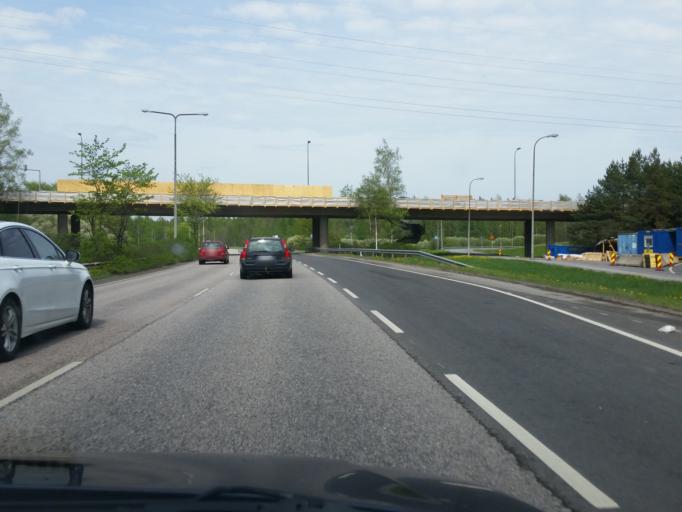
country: FI
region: Uusimaa
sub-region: Helsinki
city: Helsinki
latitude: 60.2186
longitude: 24.9090
